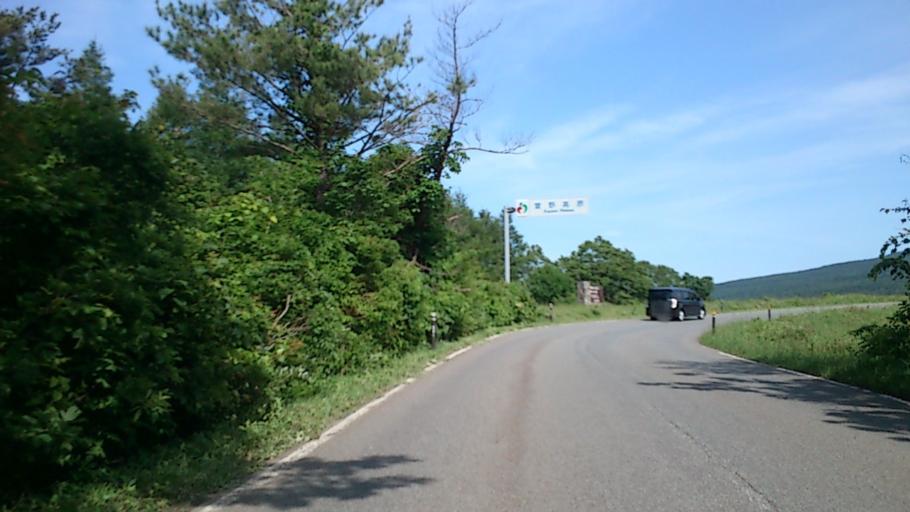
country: JP
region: Aomori
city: Aomori Shi
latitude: 40.7136
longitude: 140.8235
